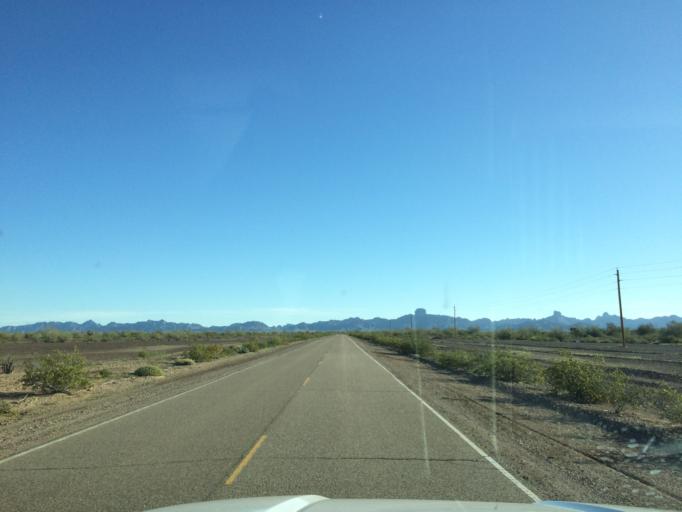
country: US
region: Arizona
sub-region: Yuma County
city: Wellton
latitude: 32.9771
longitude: -114.2764
